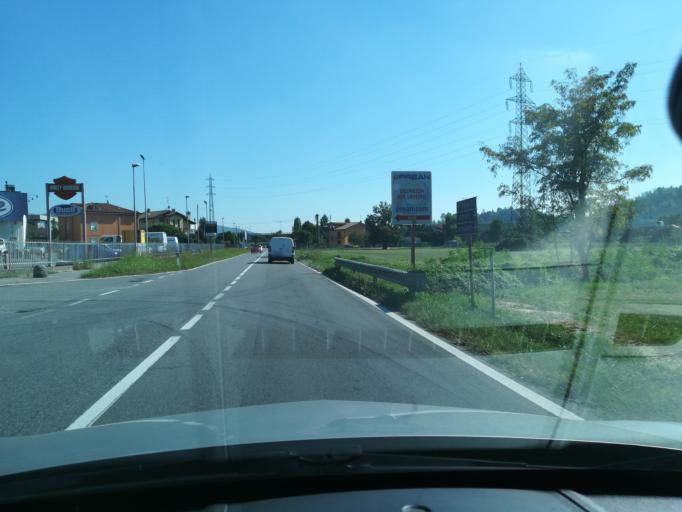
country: IT
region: Lombardy
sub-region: Provincia di Bergamo
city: San Paolo d'Argon
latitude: 45.6798
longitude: 9.7938
